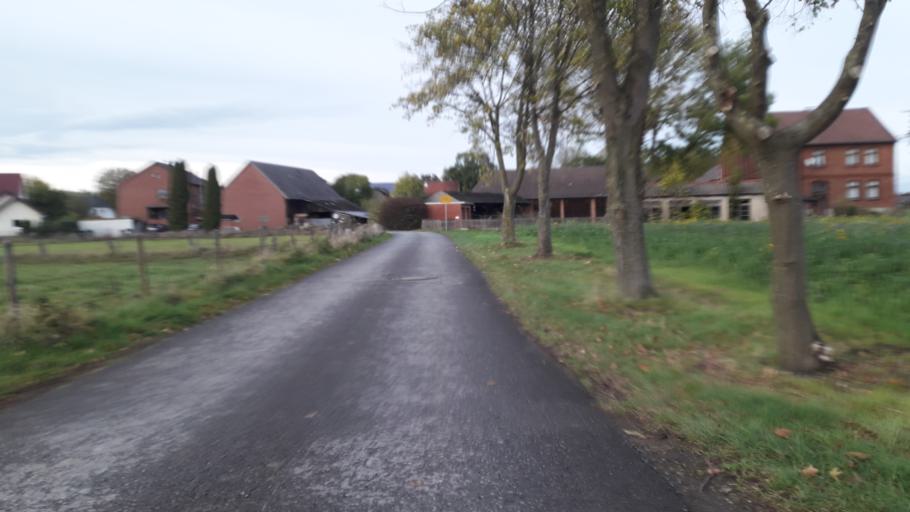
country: DE
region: North Rhine-Westphalia
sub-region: Regierungsbezirk Detmold
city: Hovelhof
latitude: 51.7374
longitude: 8.6656
